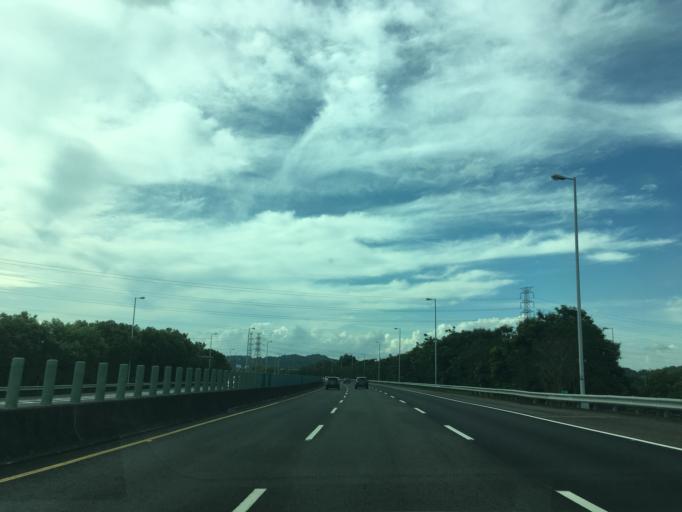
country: TW
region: Taiwan
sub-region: Chiayi
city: Jiayi Shi
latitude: 23.4984
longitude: 120.4939
